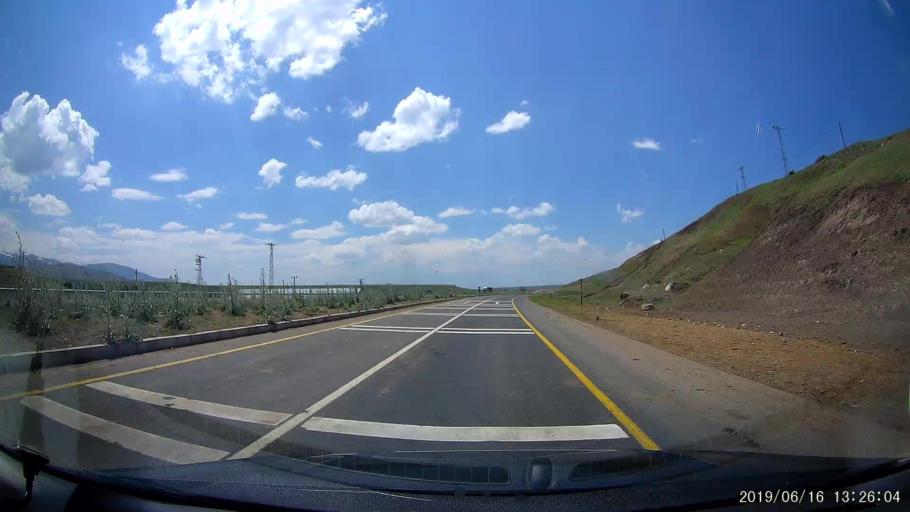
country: TR
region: Agri
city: Taslicay
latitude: 39.6570
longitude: 43.3372
